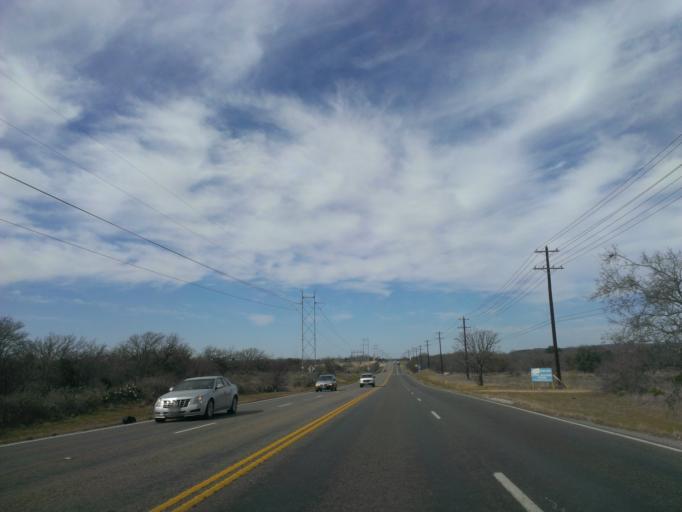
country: US
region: Texas
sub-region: Burnet County
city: Granite Shoals
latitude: 30.6071
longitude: -98.3747
